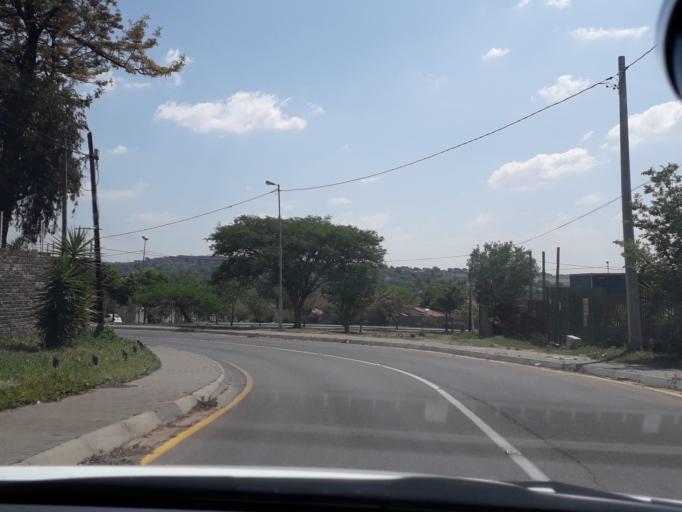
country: ZA
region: Gauteng
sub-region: City of Johannesburg Metropolitan Municipality
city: Midrand
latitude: -26.0262
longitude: 28.0632
